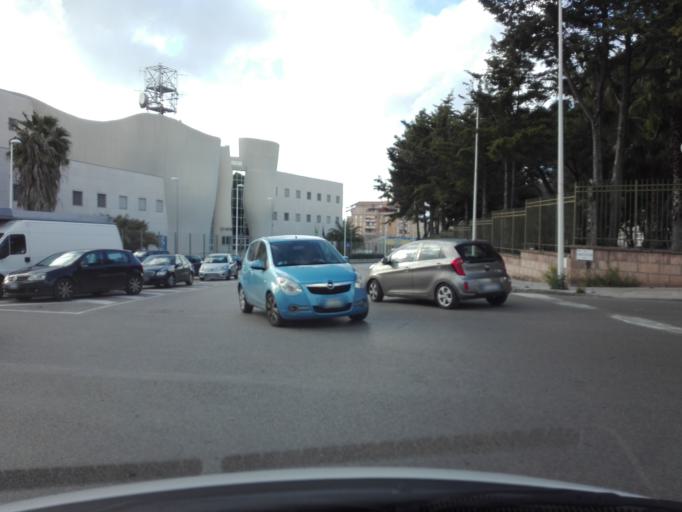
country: IT
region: Sardinia
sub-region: Provincia di Sassari
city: Sassari
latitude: 40.7354
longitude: 8.5646
